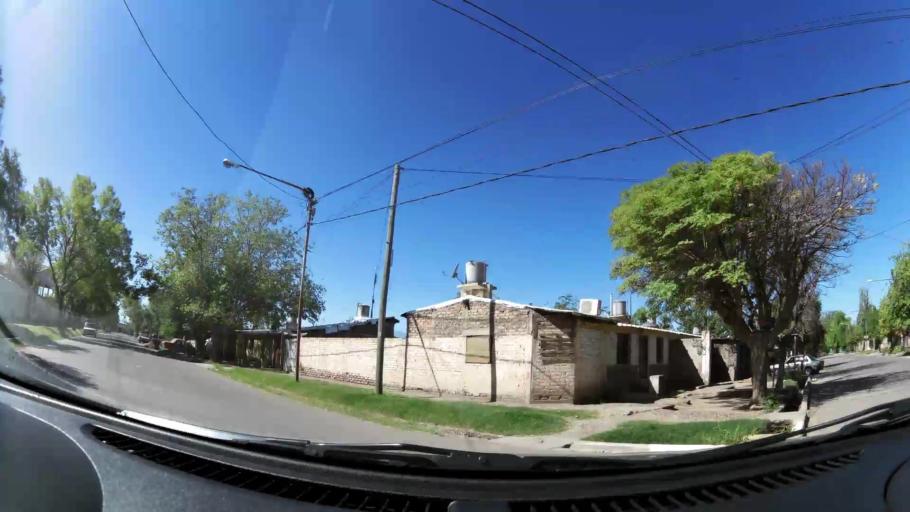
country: AR
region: Mendoza
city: Las Heras
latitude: -32.8308
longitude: -68.8197
